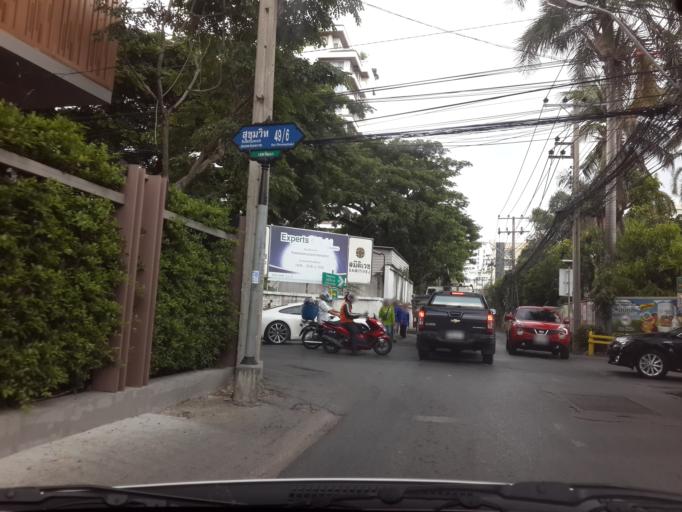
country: TH
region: Bangkok
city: Watthana
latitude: 13.7371
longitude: 100.5770
